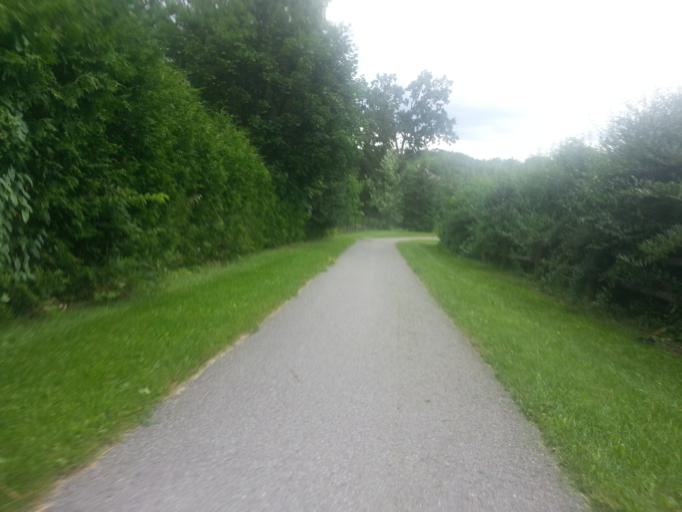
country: CA
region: Ontario
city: Bells Corners
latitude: 45.3284
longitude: -75.9258
